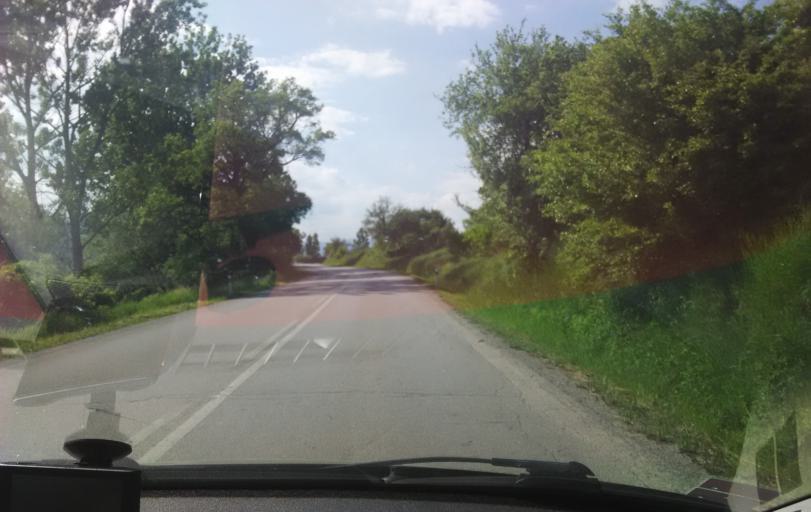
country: SK
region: Banskobystricky
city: Revuca
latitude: 48.6457
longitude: 20.2135
